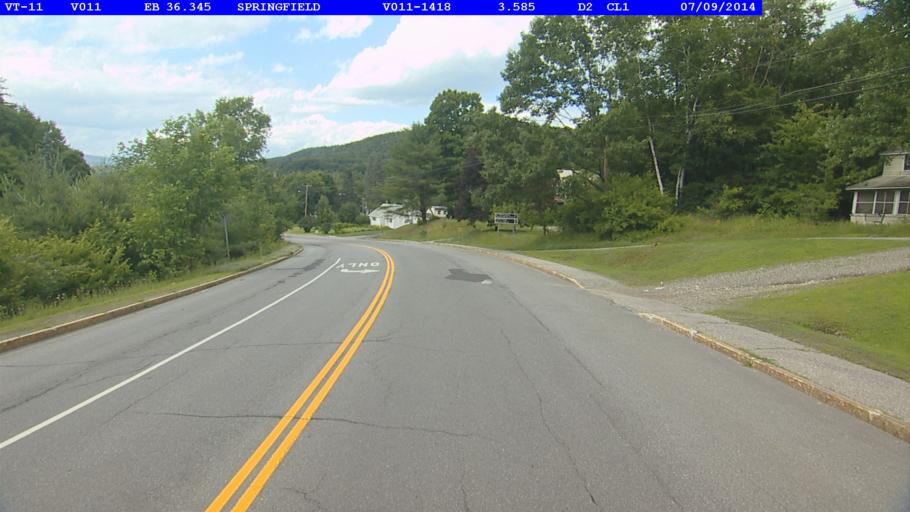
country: US
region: Vermont
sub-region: Windsor County
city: Springfield
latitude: 43.3003
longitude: -72.4945
